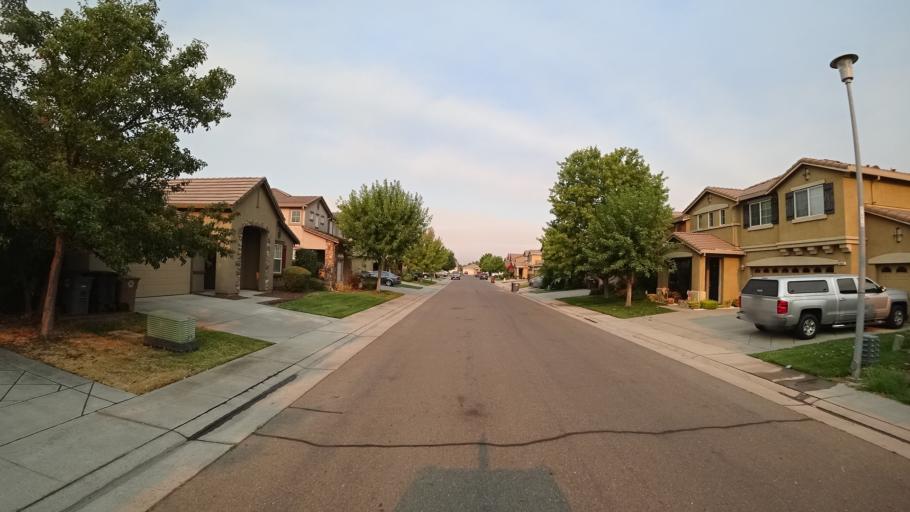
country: US
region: California
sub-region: Sacramento County
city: Laguna
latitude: 38.3933
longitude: -121.4434
